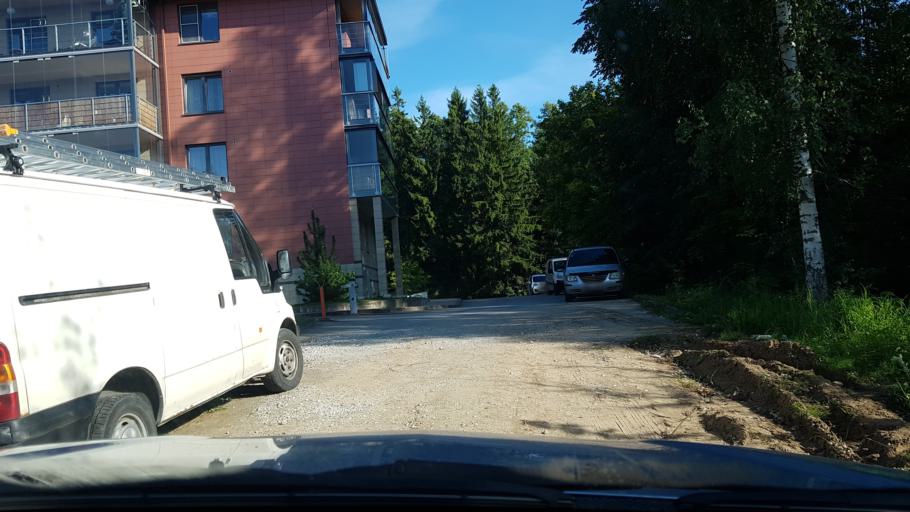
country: EE
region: Ida-Virumaa
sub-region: Narva-Joesuu linn
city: Narva-Joesuu
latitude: 59.4420
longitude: 28.0118
